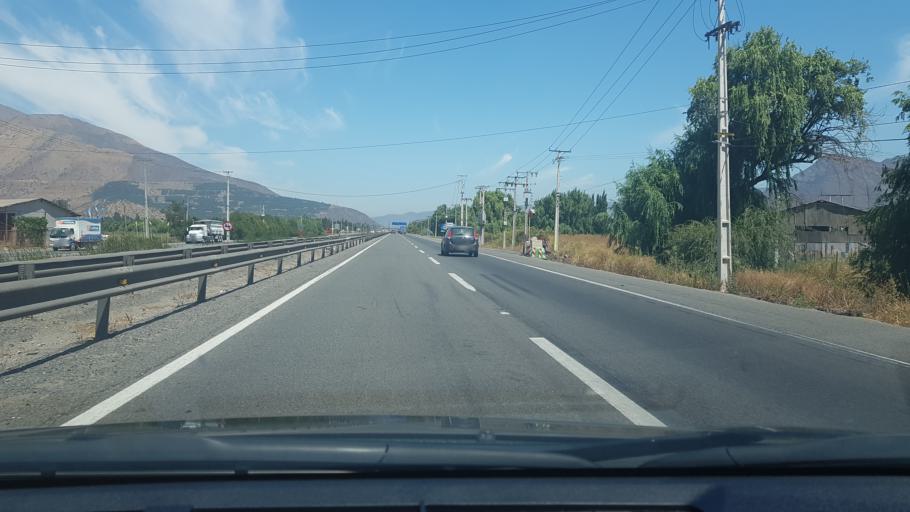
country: CL
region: Valparaiso
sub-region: Provincia de San Felipe
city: Llaillay
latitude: -32.8472
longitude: -70.9670
